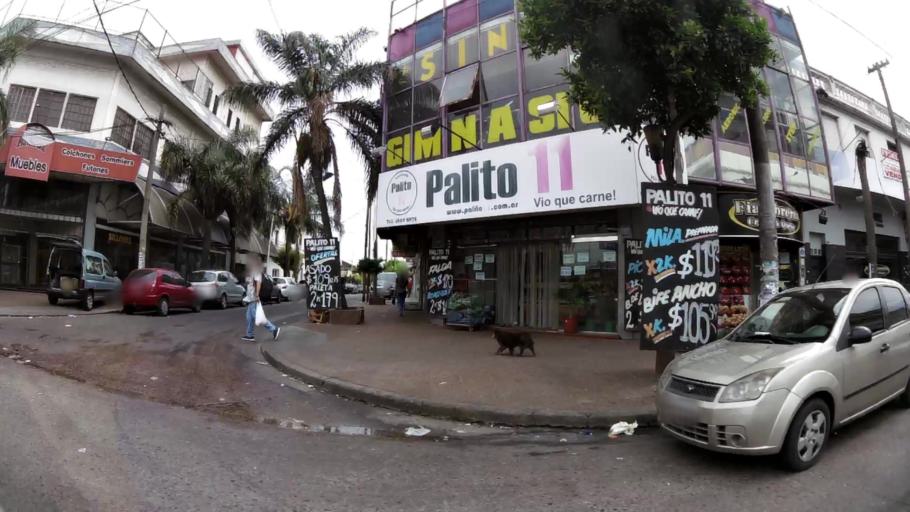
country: AR
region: Buenos Aires F.D.
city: Villa Lugano
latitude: -34.6813
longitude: -58.5130
